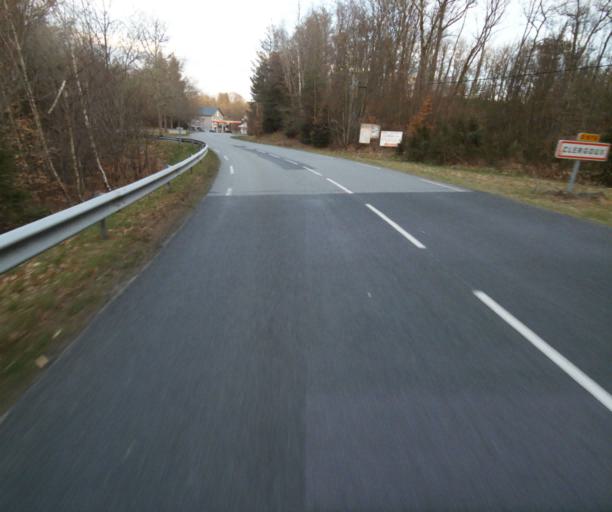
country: FR
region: Limousin
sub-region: Departement de la Correze
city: Correze
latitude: 45.2798
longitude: 1.9608
